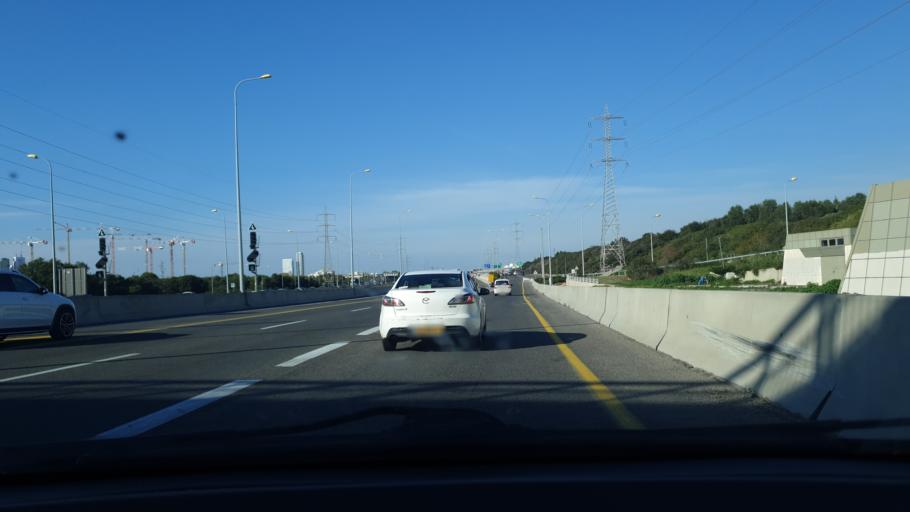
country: IL
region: Central District
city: Rishon LeZiyyon
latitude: 31.9796
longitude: 34.7563
